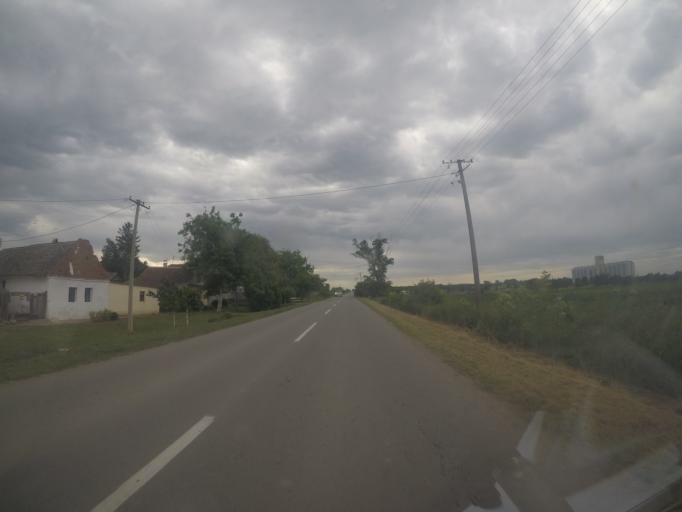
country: RS
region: Autonomna Pokrajina Vojvodina
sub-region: Juznobanatski Okrug
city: Opovo
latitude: 45.0416
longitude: 20.4440
